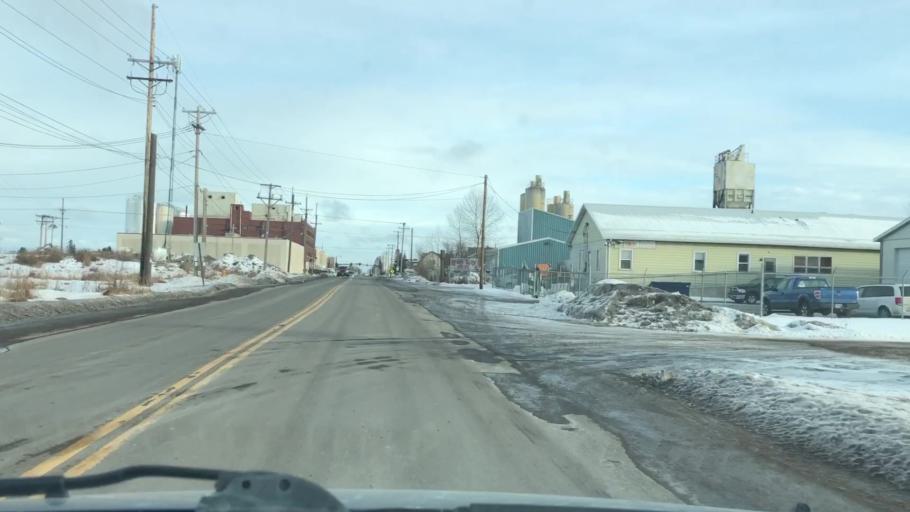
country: US
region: Wisconsin
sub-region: Douglas County
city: Superior
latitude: 46.7279
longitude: -92.1093
